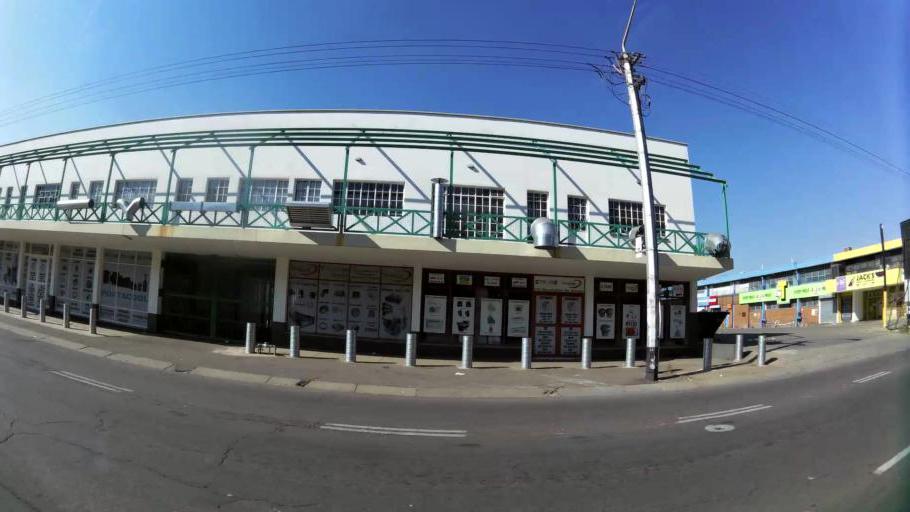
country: ZA
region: Gauteng
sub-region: City of Tshwane Metropolitan Municipality
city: Pretoria
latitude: -25.7211
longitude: 28.2028
